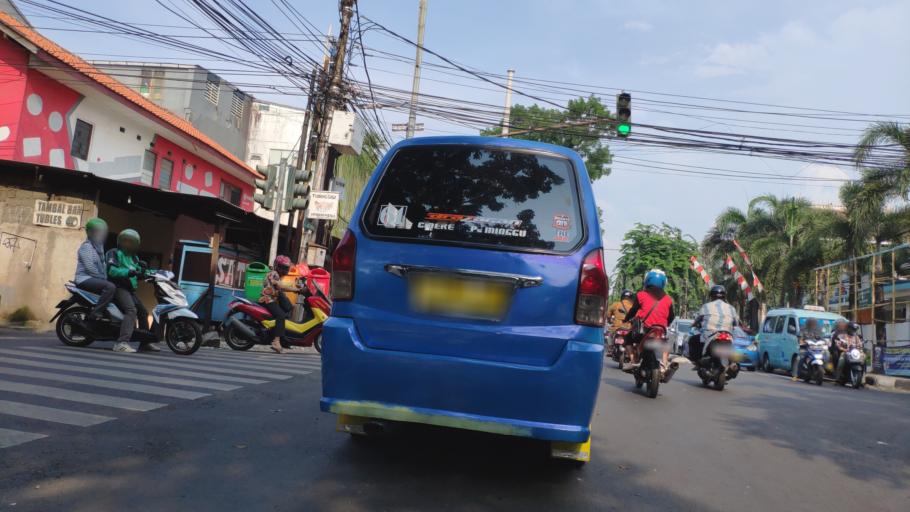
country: ID
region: Jakarta Raya
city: Jakarta
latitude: -6.2860
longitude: 106.8291
